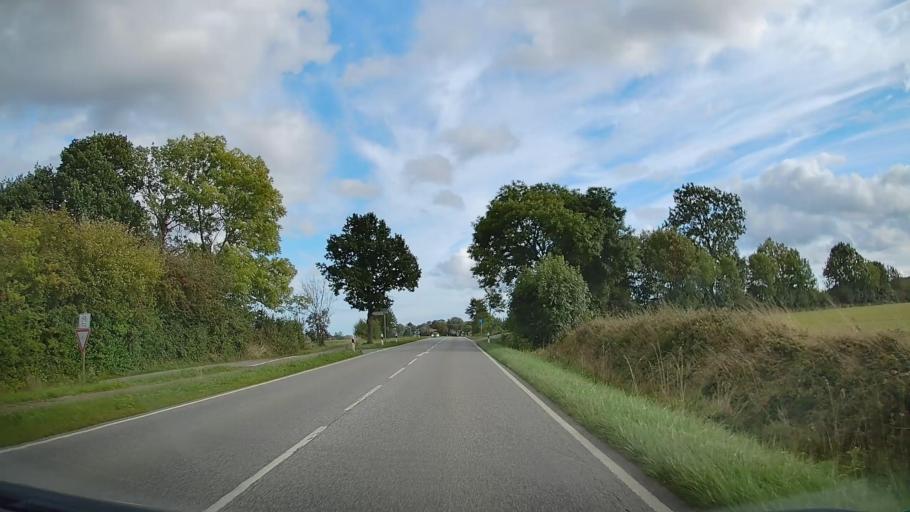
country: DE
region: Schleswig-Holstein
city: Stangheck
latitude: 54.7490
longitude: 9.8582
